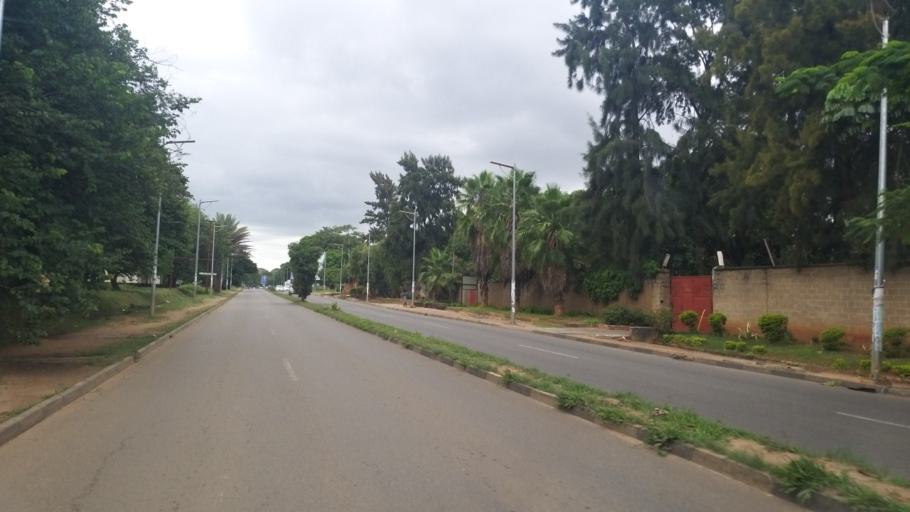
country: ZM
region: Lusaka
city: Lusaka
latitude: -15.4151
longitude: 28.3100
